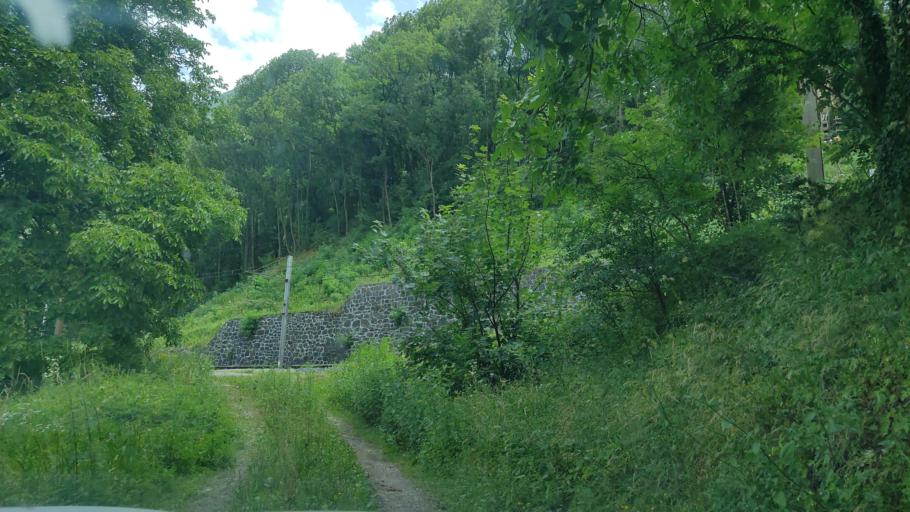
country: FR
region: Rhone-Alpes
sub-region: Departement de la Savoie
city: Saint-Remy-de-Maurienne
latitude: 45.4258
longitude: 6.2754
